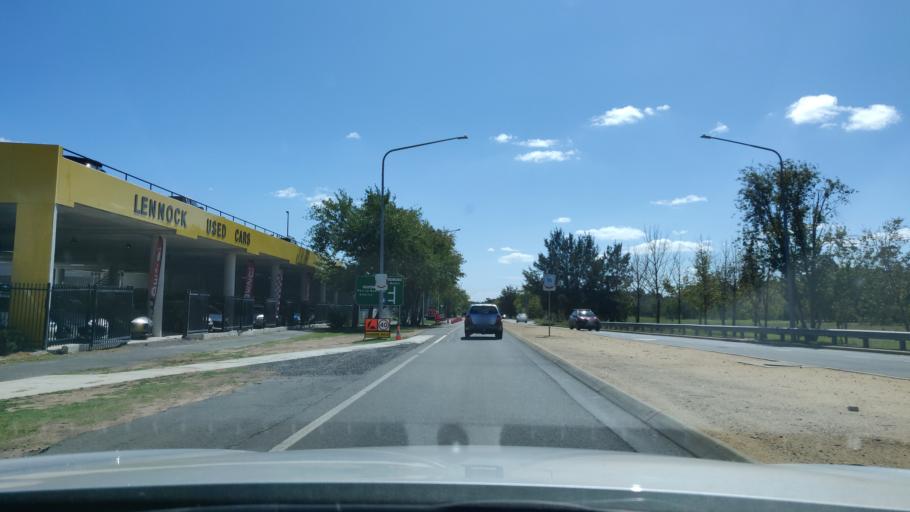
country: AU
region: Australian Capital Territory
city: Forrest
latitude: -35.3568
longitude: 149.0915
